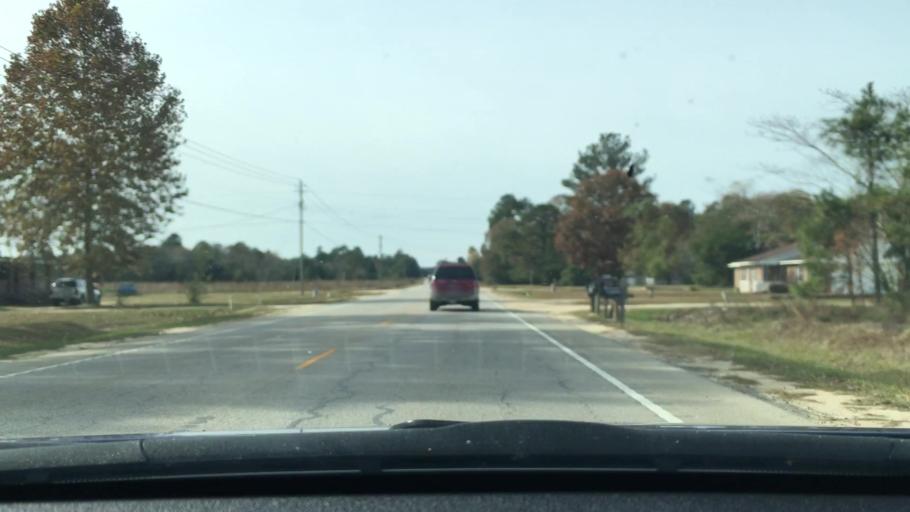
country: US
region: South Carolina
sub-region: Sumter County
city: Cherryvale
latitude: 33.9369
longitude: -80.4615
